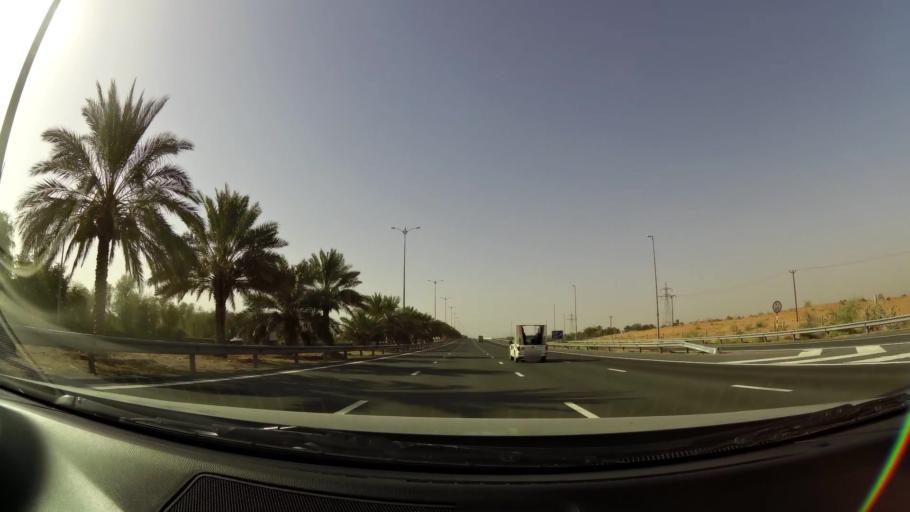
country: OM
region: Al Buraimi
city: Al Buraymi
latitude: 24.4331
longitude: 55.7871
